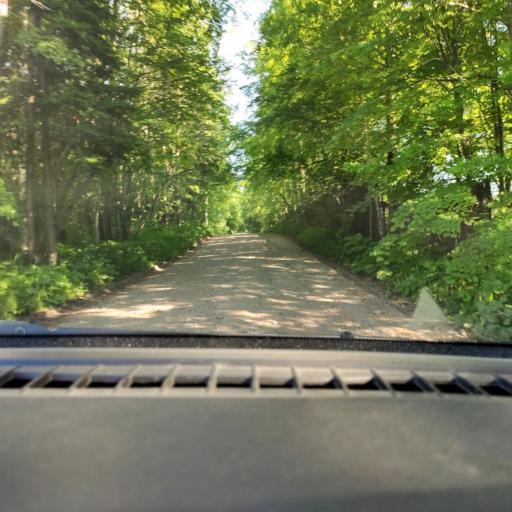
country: RU
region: Perm
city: Overyata
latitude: 58.1243
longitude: 55.8787
